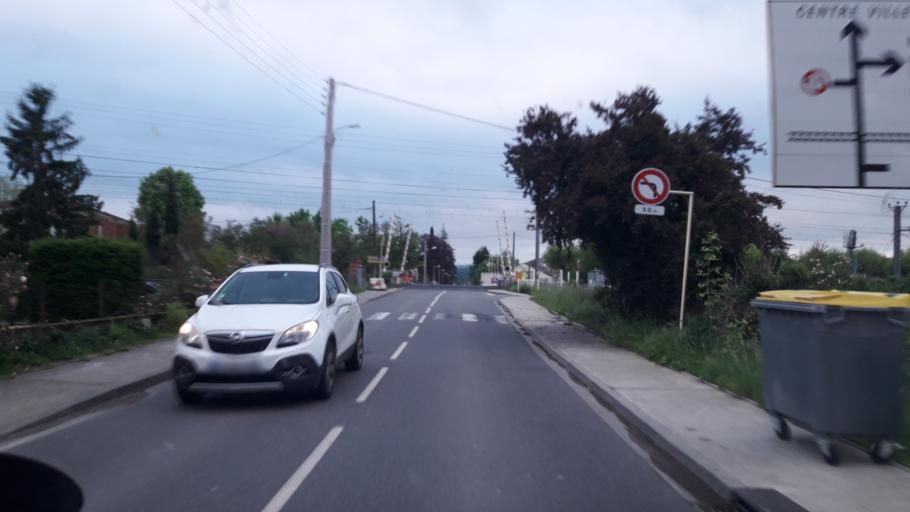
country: FR
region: Midi-Pyrenees
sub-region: Departement de la Haute-Garonne
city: Cazeres
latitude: 43.2143
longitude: 1.0854
